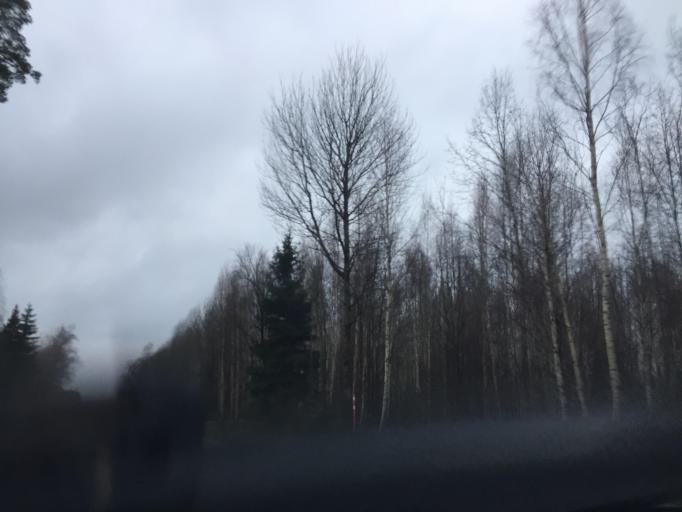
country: LV
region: Salacgrivas
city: Salacgriva
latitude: 57.7625
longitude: 24.5533
